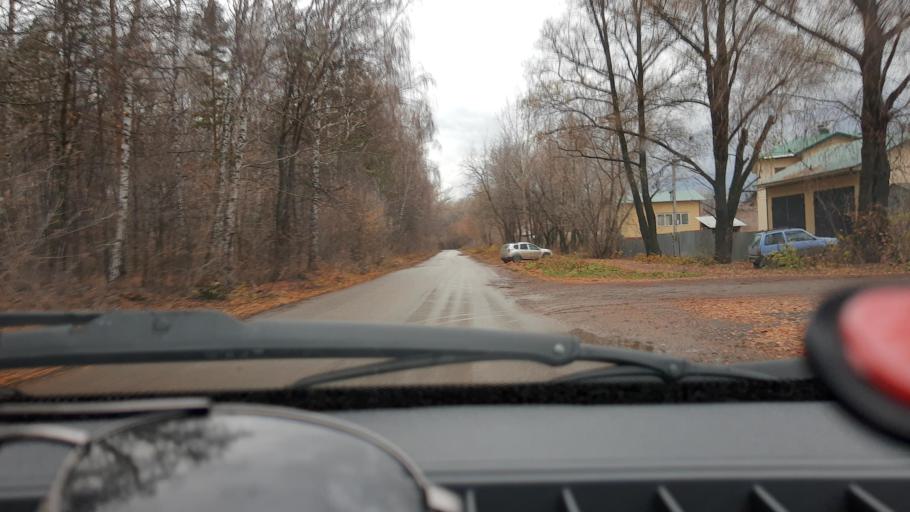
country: RU
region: Bashkortostan
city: Ufa
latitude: 54.7891
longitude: 56.1587
